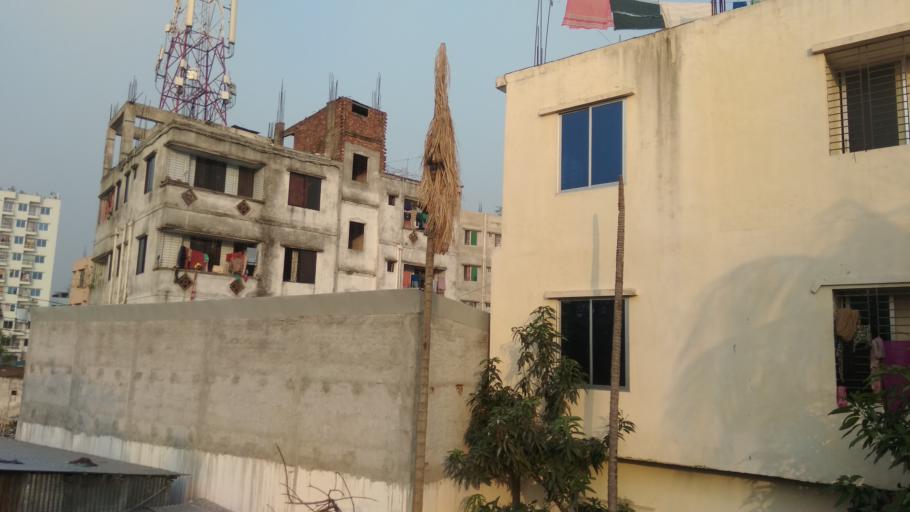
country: BD
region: Dhaka
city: Tungi
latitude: 23.8569
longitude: 90.4279
